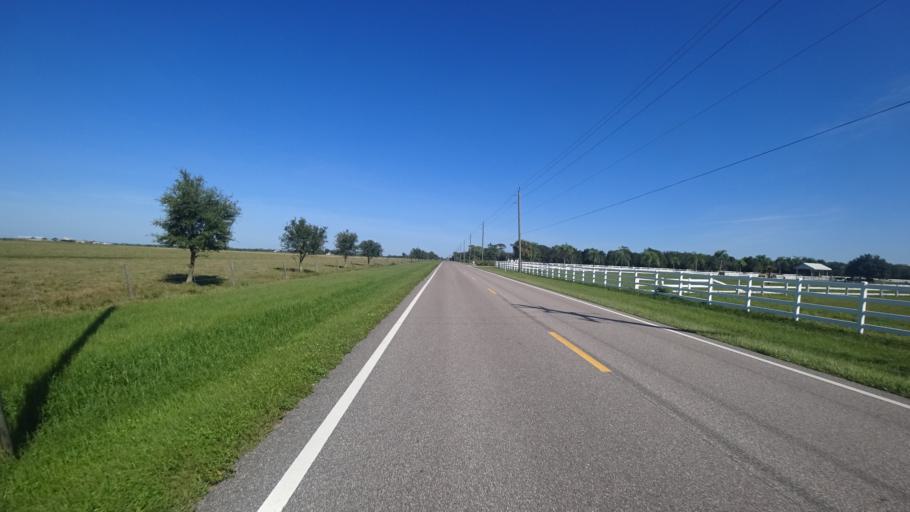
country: US
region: Florida
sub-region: Sarasota County
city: Lake Sarasota
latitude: 27.3636
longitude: -82.2684
